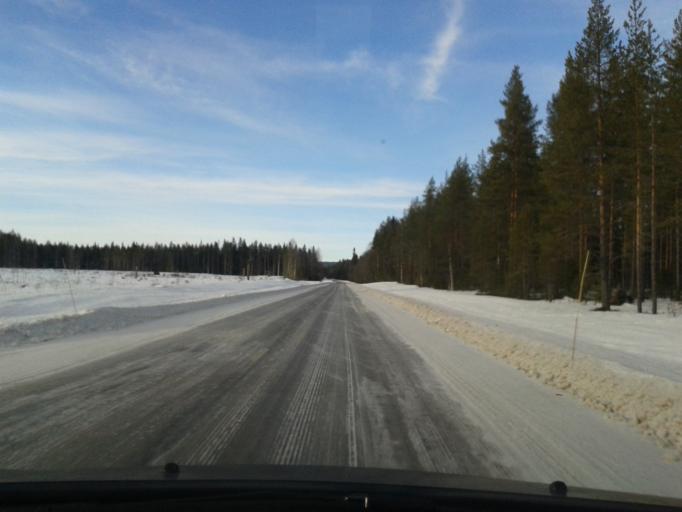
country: SE
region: Vaesternorrland
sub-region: OErnskoeldsviks Kommun
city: Bredbyn
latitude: 63.5972
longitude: 17.9147
